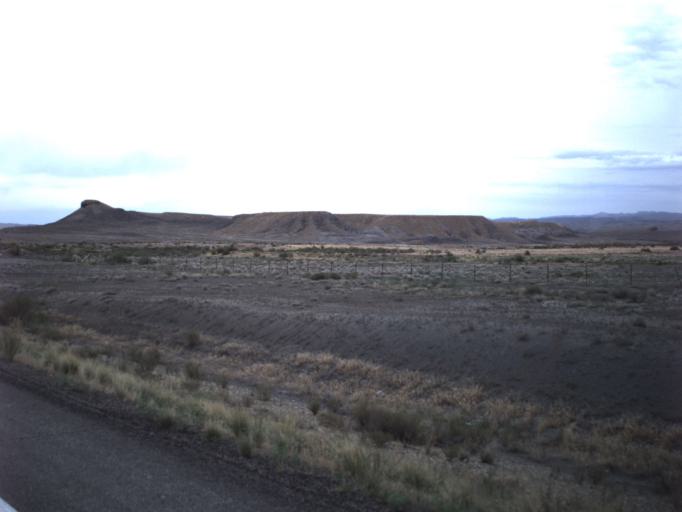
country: US
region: Utah
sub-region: Carbon County
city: East Carbon City
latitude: 39.3489
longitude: -110.3786
